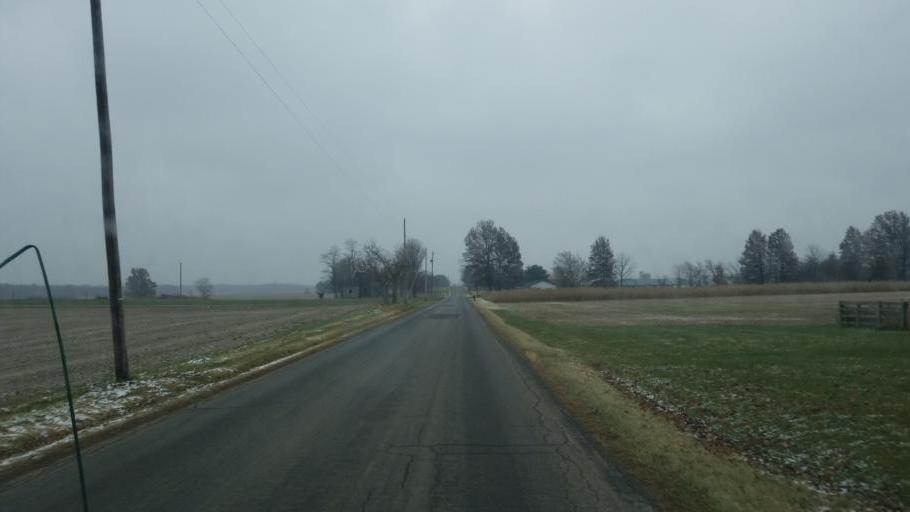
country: US
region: Ohio
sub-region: Huron County
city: Greenwich
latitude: 40.9754
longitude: -82.5512
